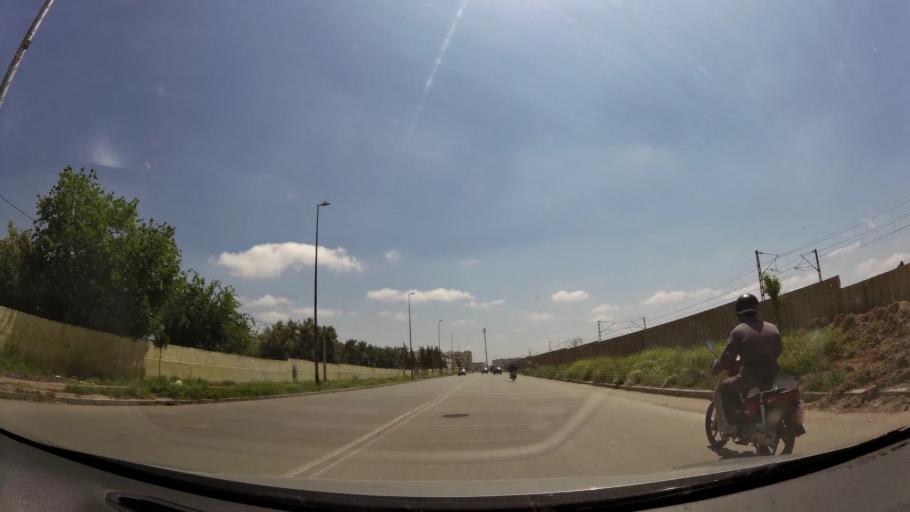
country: MA
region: Fes-Boulemane
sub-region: Fes
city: Fes
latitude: 34.0181
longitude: -5.0419
